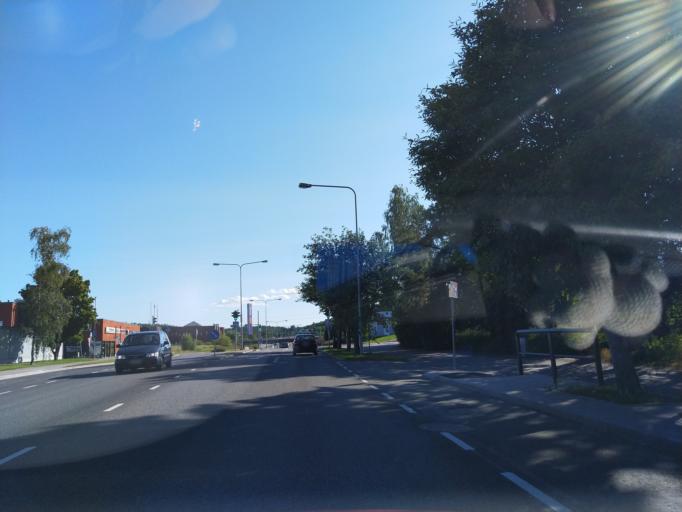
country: FI
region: Varsinais-Suomi
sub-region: Turku
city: Turku
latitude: 60.4416
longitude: 22.3229
